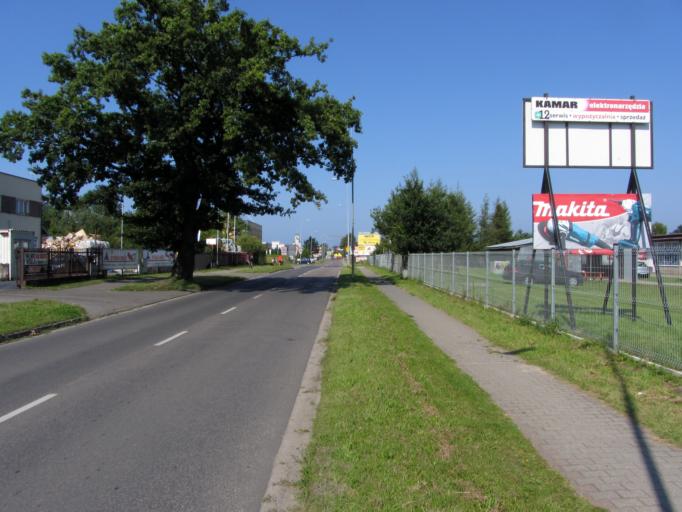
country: PL
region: West Pomeranian Voivodeship
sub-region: Powiat kolobrzeski
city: Kolobrzeg
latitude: 54.1691
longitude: 15.5504
